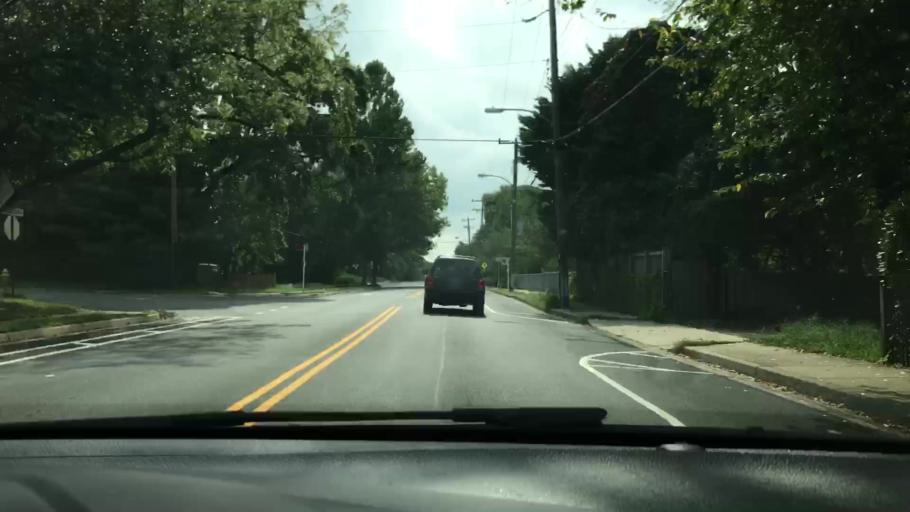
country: US
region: Virginia
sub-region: Fairfax County
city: Seven Corners
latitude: 38.8871
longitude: -77.1456
